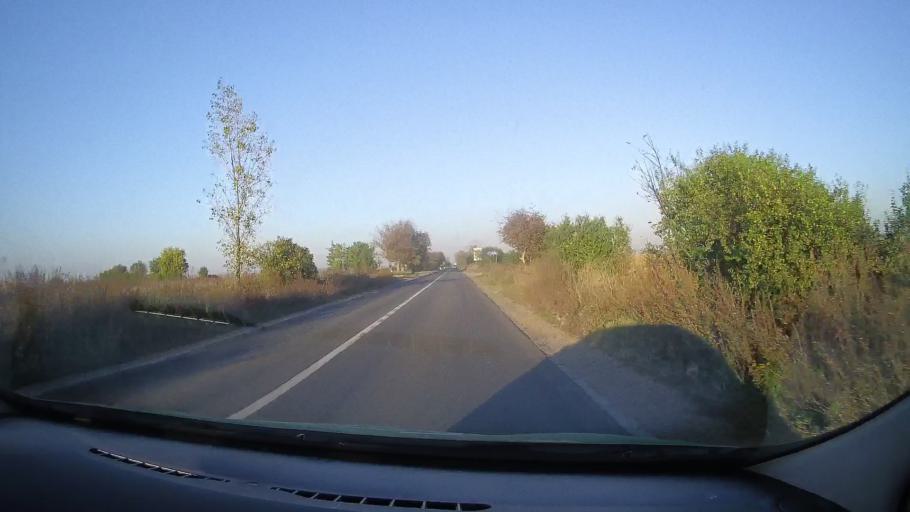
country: RO
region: Bihor
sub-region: Comuna Cetariu
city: Cetariu
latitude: 47.1829
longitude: 21.9816
